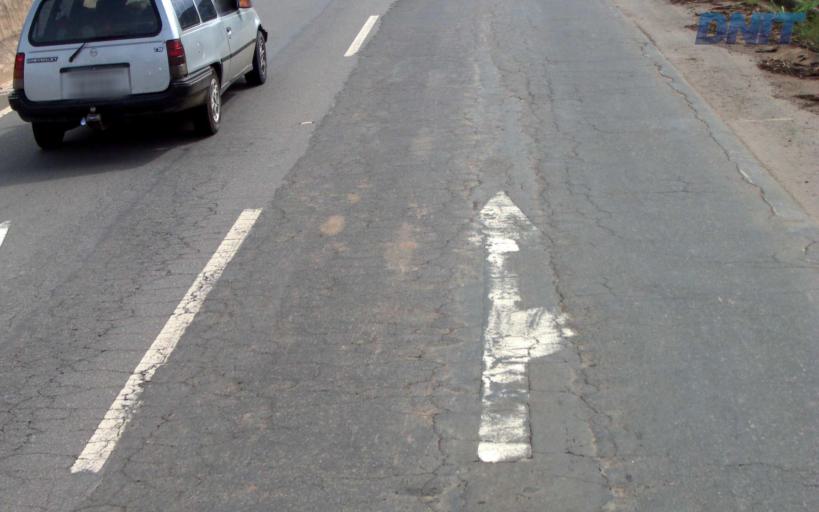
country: BR
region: Minas Gerais
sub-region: Ipaba
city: Ipaba
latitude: -19.3199
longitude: -42.4046
